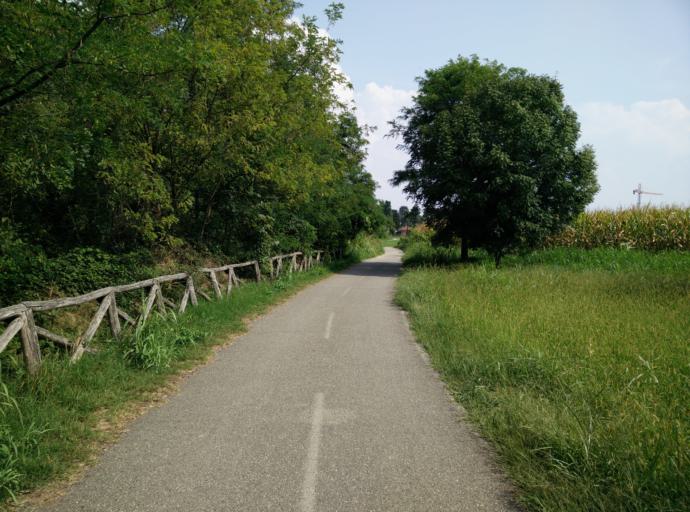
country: IT
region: Piedmont
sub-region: Provincia di Torino
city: Pasta
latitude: 45.0157
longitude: 7.5483
